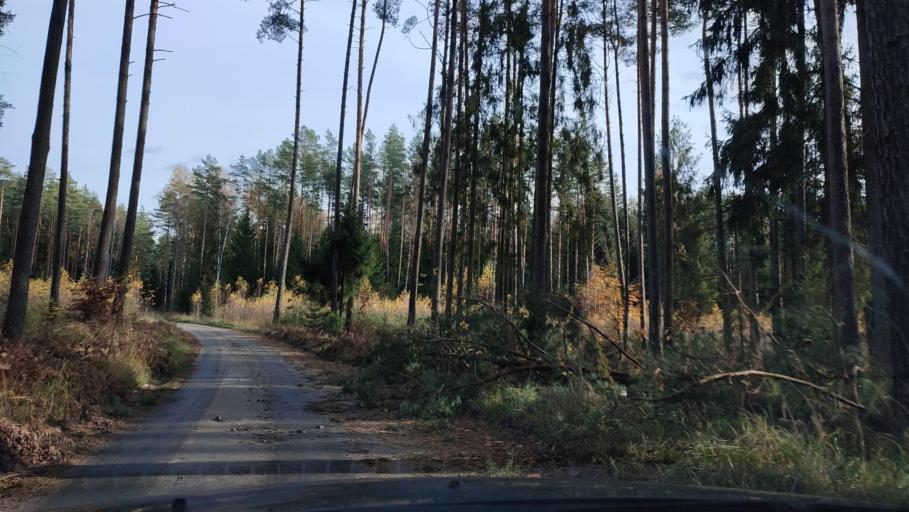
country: PL
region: Warmian-Masurian Voivodeship
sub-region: Powiat szczycienski
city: Szczytno
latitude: 53.5244
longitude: 20.9002
